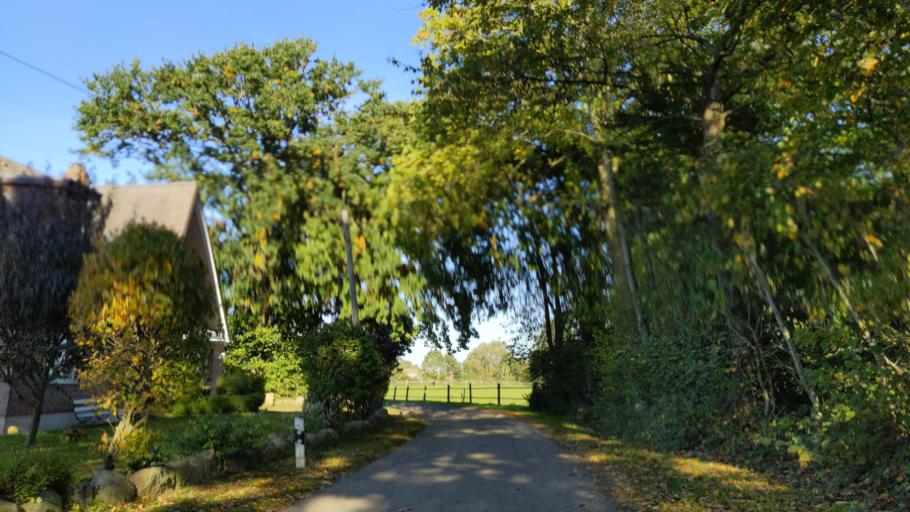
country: DE
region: Schleswig-Holstein
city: Ahrensbok
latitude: 54.0142
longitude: 10.6196
